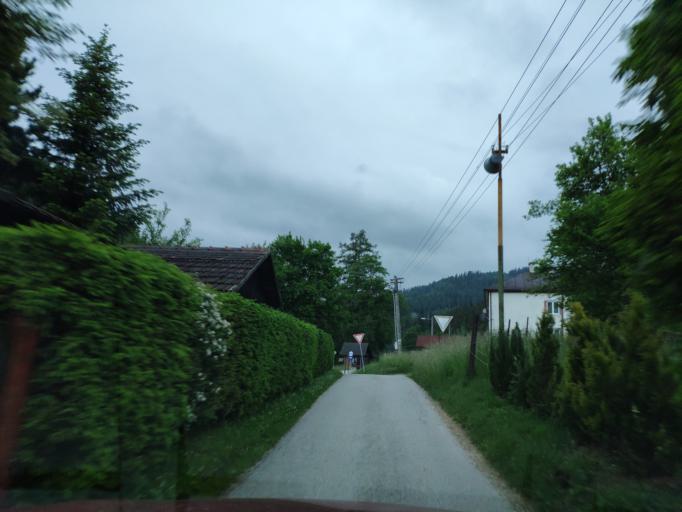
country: SK
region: Kosicky
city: Medzev
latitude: 48.7274
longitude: 20.7199
